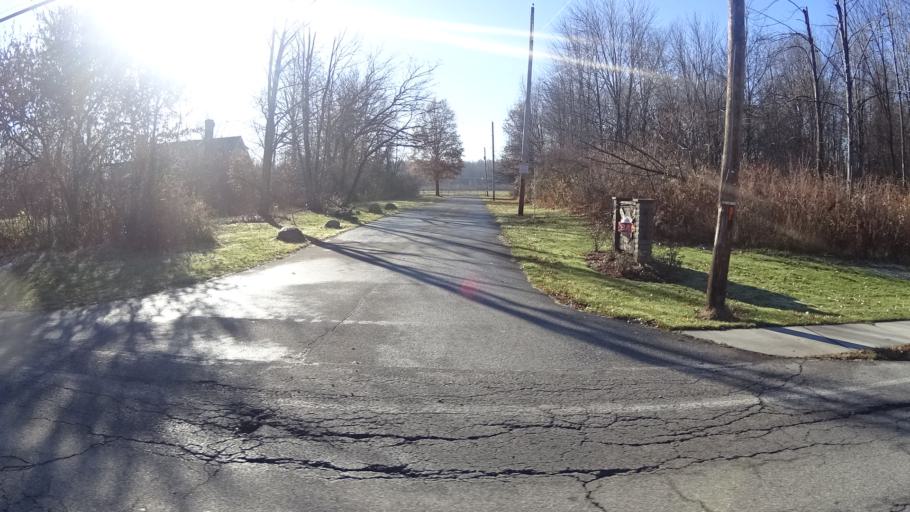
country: US
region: Ohio
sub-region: Lorain County
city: Sheffield Lake
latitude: 41.4823
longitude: -82.0894
